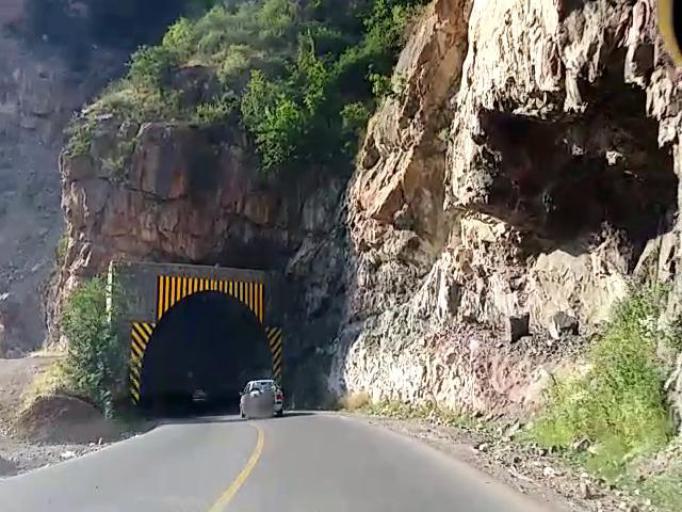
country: IR
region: Mazandaran
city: Chalus
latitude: 36.2601
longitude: 51.2746
